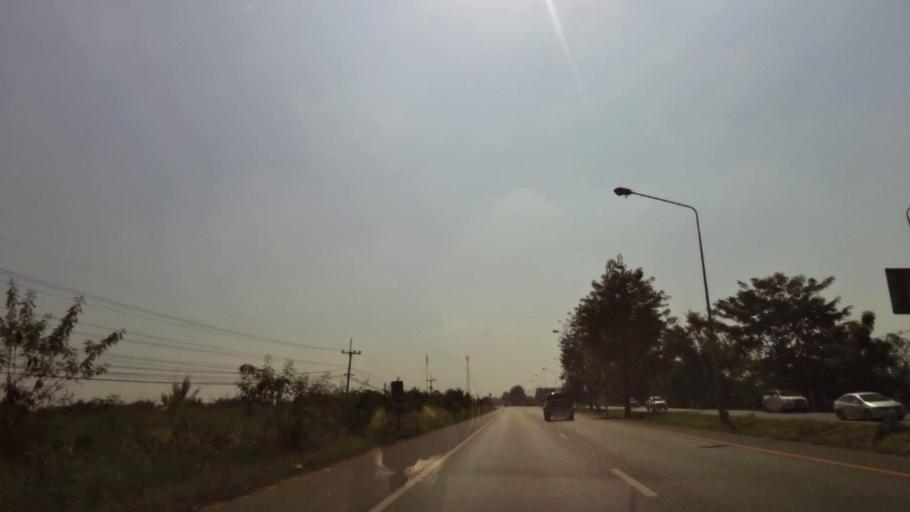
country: TH
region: Phichit
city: Wachira Barami
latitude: 16.3510
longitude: 100.1288
